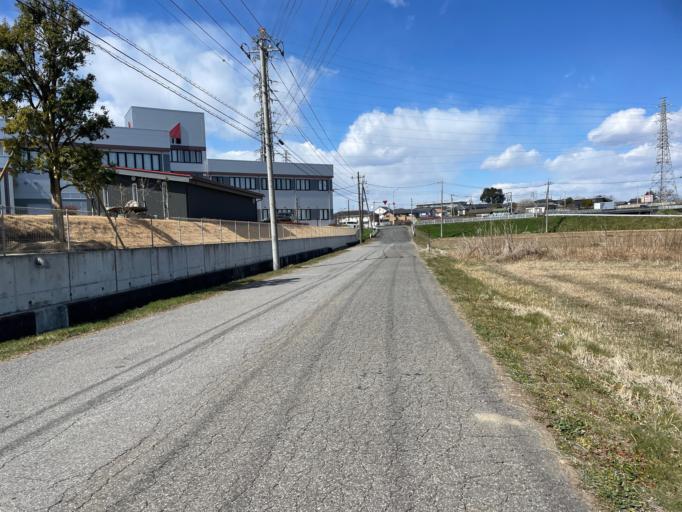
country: JP
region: Saitama
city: Sakado
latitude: 35.9929
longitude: 139.4052
